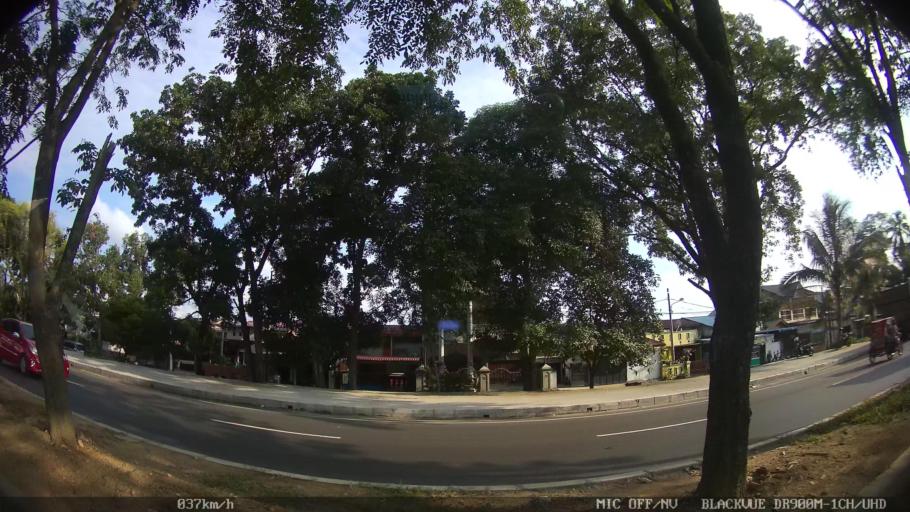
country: ID
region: North Sumatra
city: Sunggal
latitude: 3.6155
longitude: 98.6292
